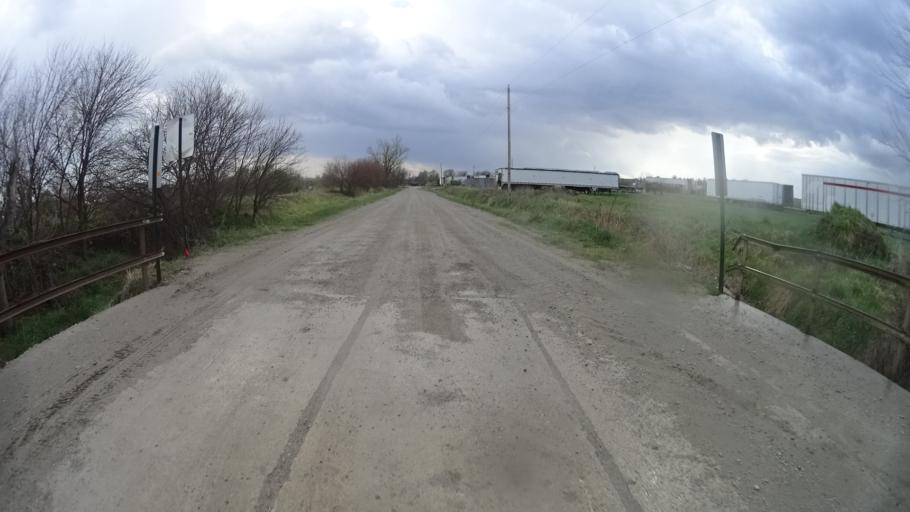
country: US
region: Nebraska
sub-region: Sarpy County
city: Offutt Air Force Base
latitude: 41.0771
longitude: -95.9212
